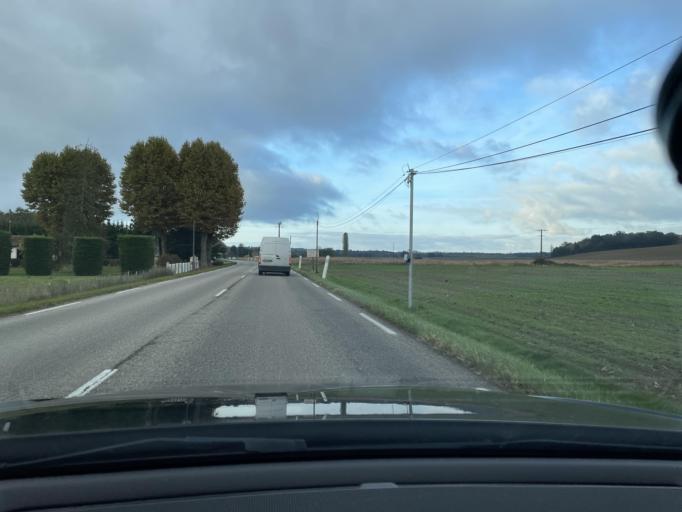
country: FR
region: Aquitaine
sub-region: Departement du Lot-et-Garonne
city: Casteljaloux
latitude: 44.3672
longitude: 0.1071
